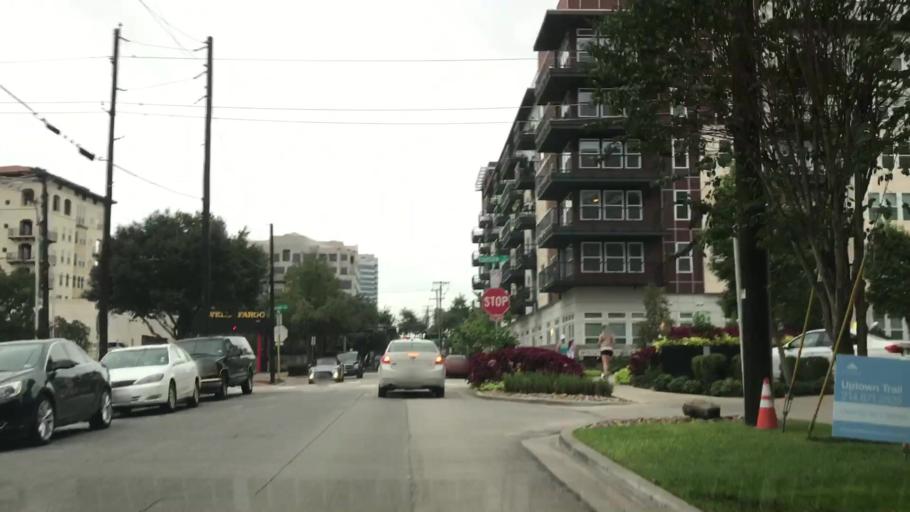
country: US
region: Texas
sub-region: Dallas County
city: Dallas
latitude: 32.8004
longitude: -96.8064
